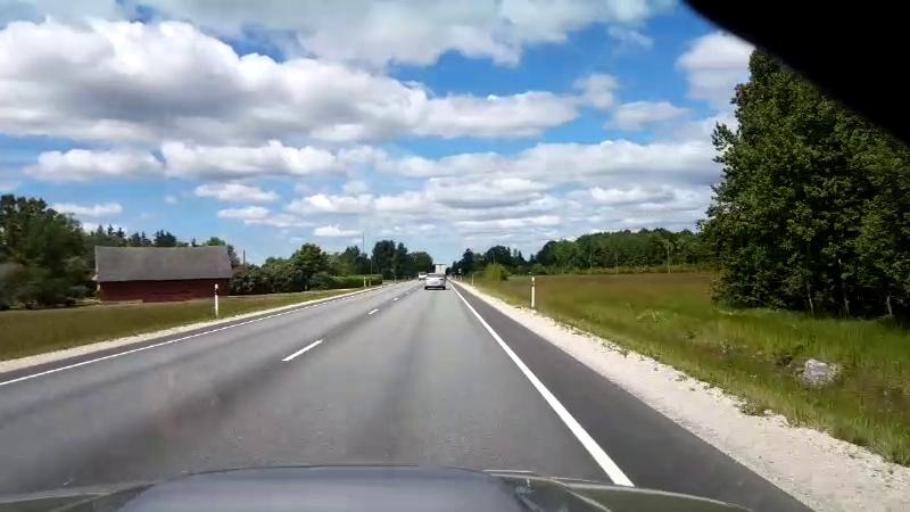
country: EE
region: Paernumaa
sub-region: Halinga vald
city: Parnu-Jaagupi
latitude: 58.6514
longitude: 24.4793
